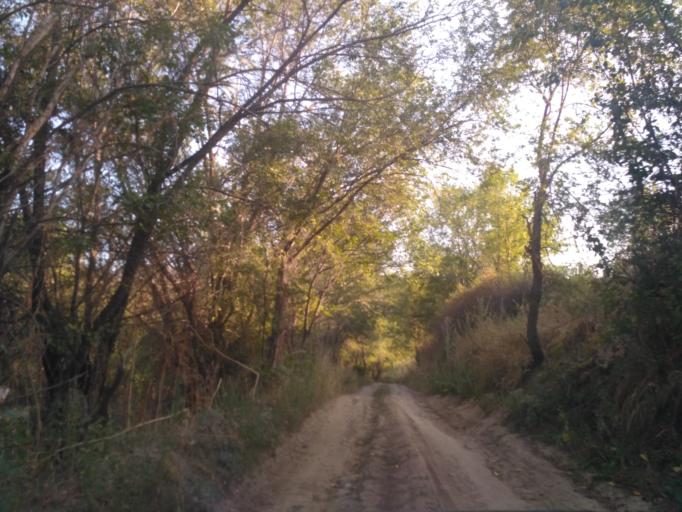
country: KZ
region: Almaty Oblysy
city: Burunday
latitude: 43.1534
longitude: 76.3709
